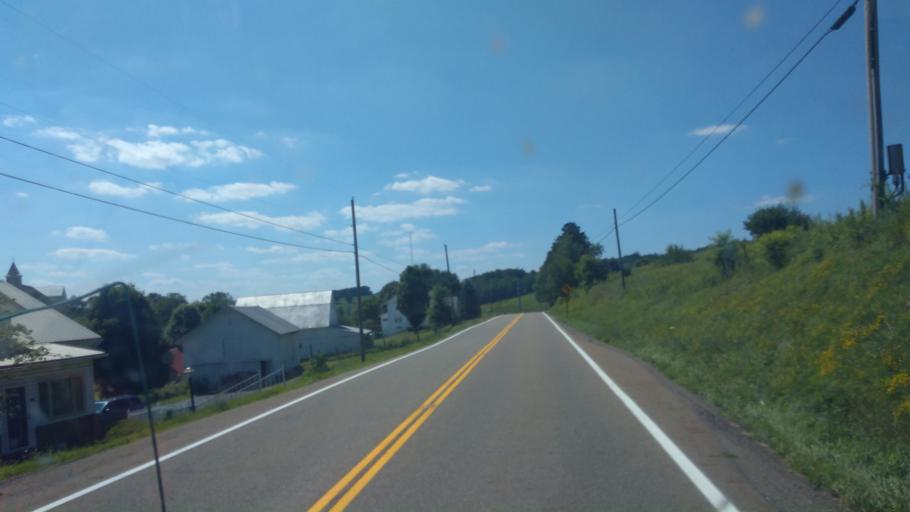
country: US
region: Ohio
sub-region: Carroll County
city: Carrollton
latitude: 40.5779
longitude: -81.0983
